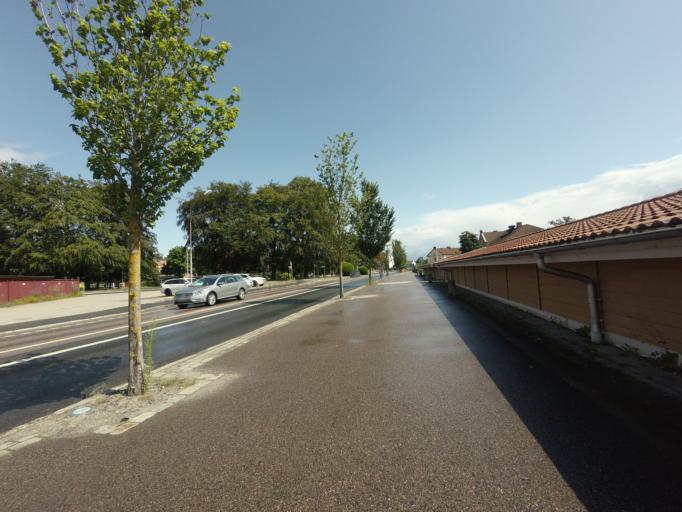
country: SE
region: Skane
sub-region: Osby Kommun
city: Osby
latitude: 56.3788
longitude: 13.9952
